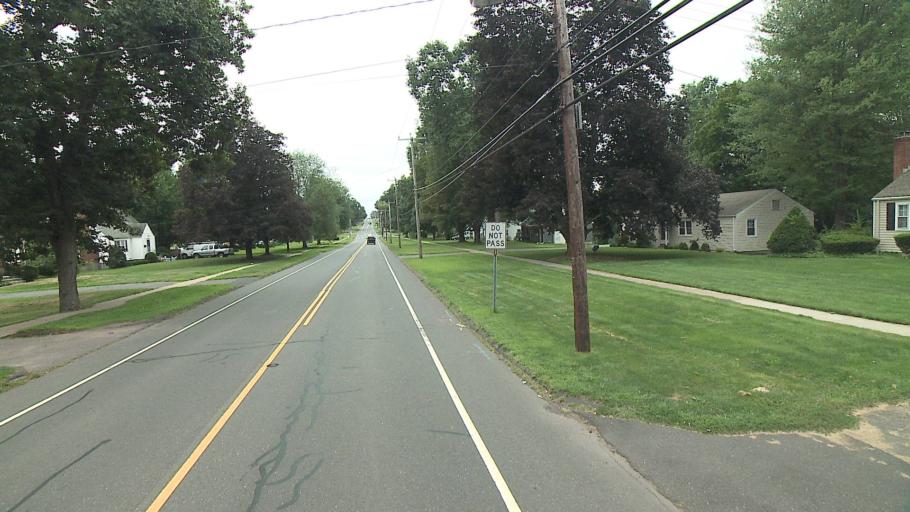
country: US
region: Connecticut
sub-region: Hartford County
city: Wethersfield
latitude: 41.6825
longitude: -72.6648
